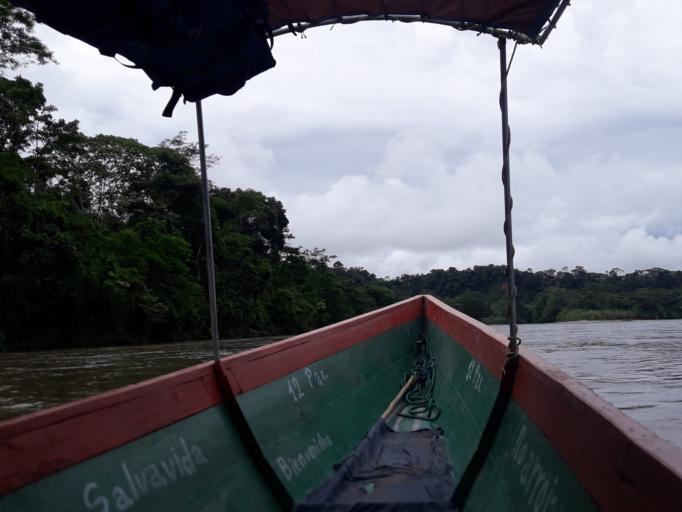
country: EC
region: Napo
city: Tena
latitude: -1.0359
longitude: -77.6609
